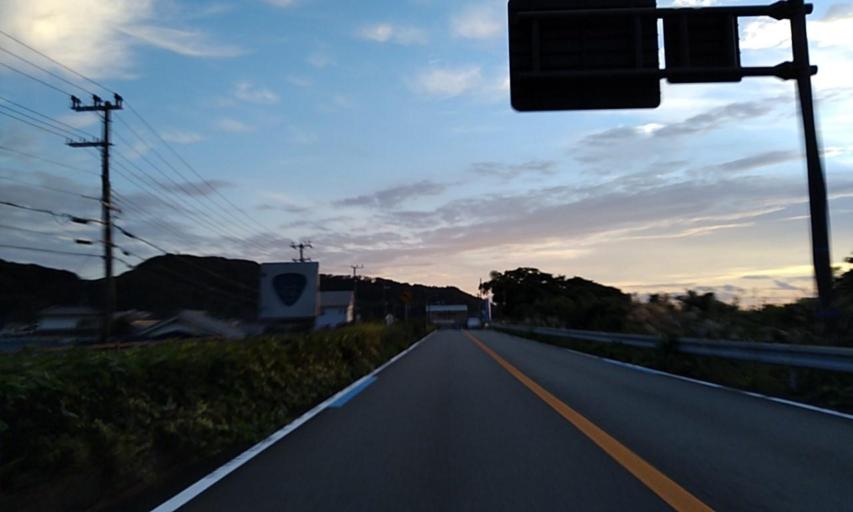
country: JP
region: Wakayama
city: Tanabe
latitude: 33.6466
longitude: 135.4013
